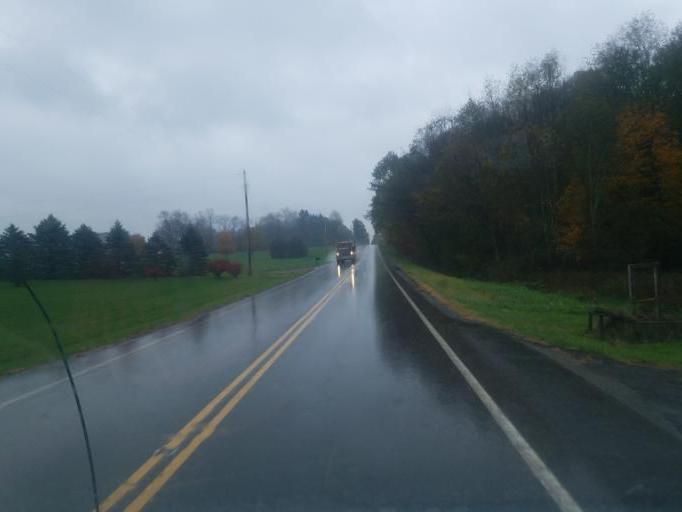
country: US
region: Ohio
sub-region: Licking County
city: Utica
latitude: 40.2557
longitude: -82.3357
